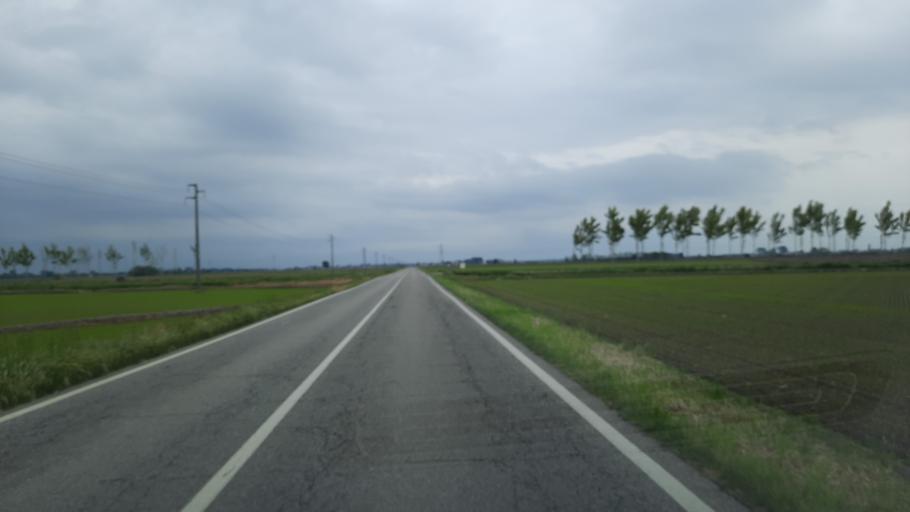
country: IT
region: Lombardy
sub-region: Provincia di Pavia
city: Robbio
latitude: 45.2761
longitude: 8.6089
